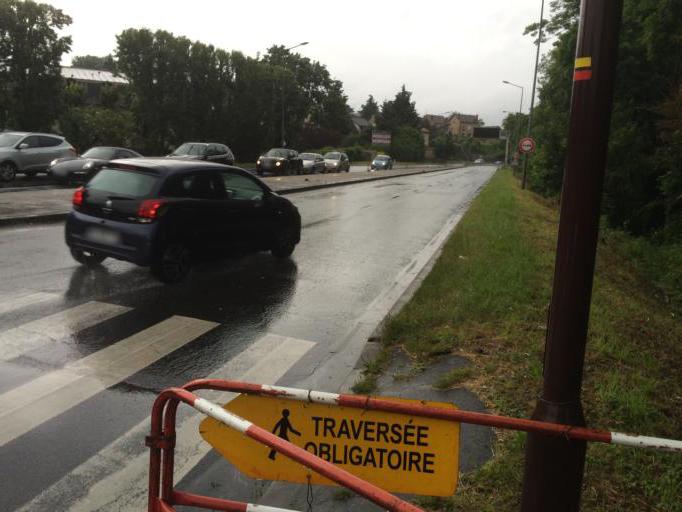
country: FR
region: Ile-de-France
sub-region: Departement de l'Essonne
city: Villemoisson-sur-Orge
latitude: 48.6728
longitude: 2.3357
